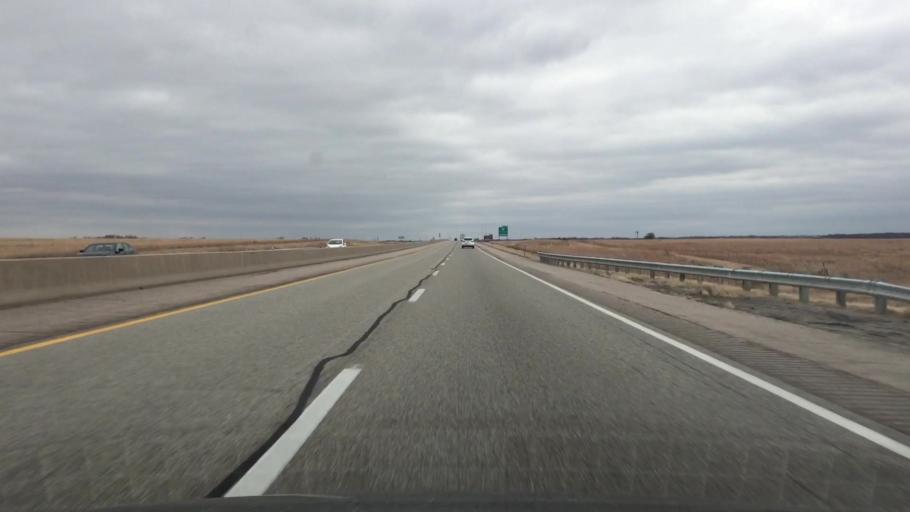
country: US
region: Kansas
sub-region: Butler County
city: El Dorado
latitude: 37.8907
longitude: -96.8377
